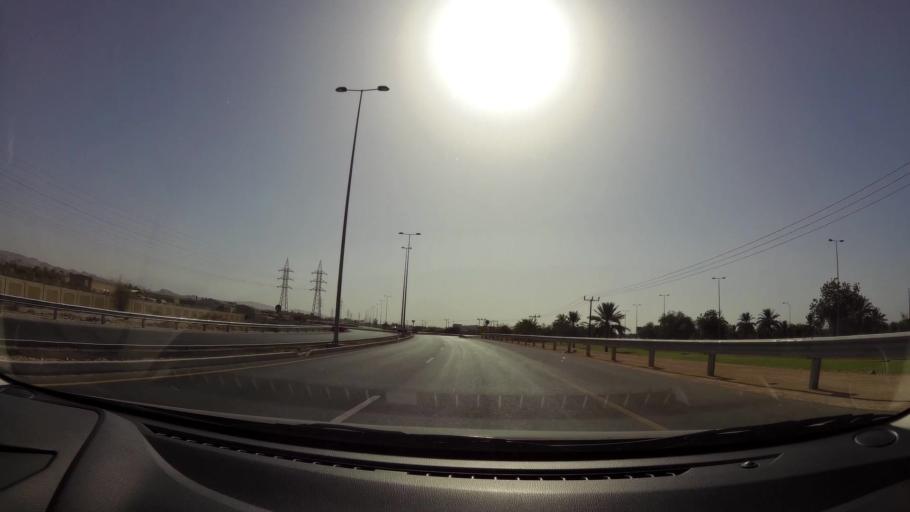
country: OM
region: Muhafazat Masqat
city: As Sib al Jadidah
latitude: 23.5824
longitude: 58.2643
